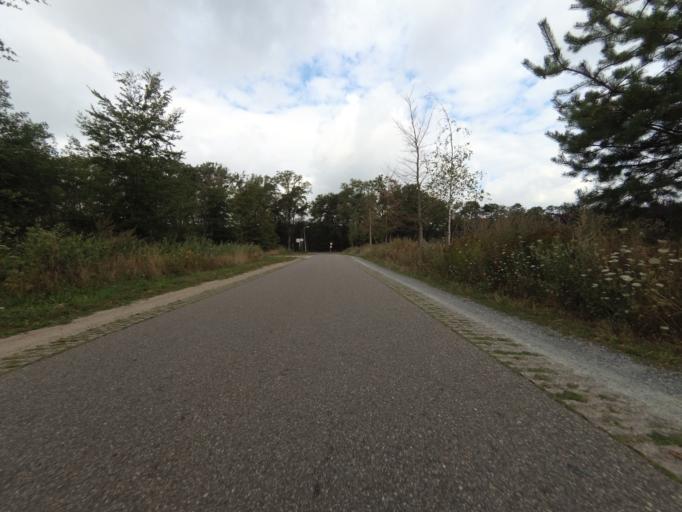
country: NL
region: Overijssel
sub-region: Gemeente Borne
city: Borne
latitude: 52.3168
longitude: 6.7713
